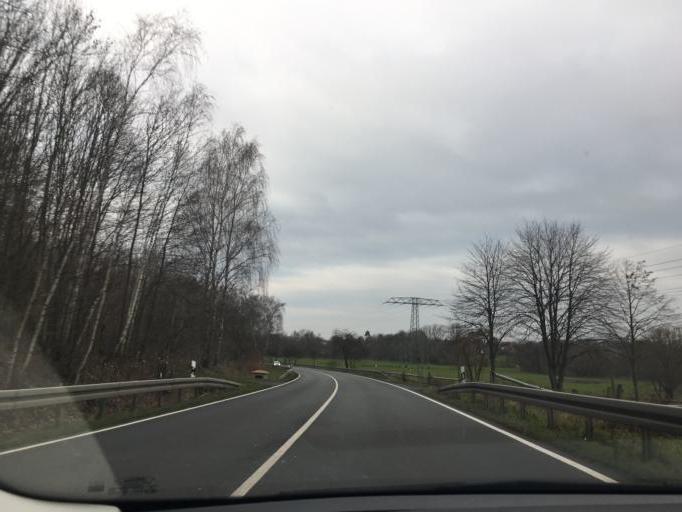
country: DE
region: Saxony
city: Kitzscher
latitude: 51.1482
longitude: 12.5300
